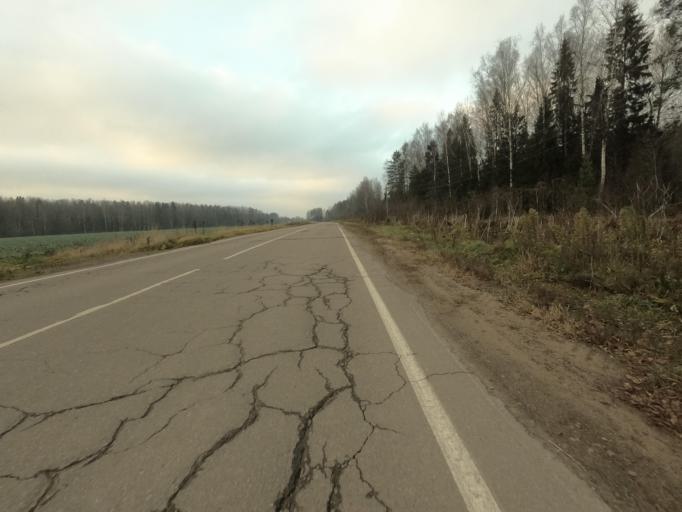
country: RU
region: Leningrad
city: Mga
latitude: 59.7984
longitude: 31.0009
